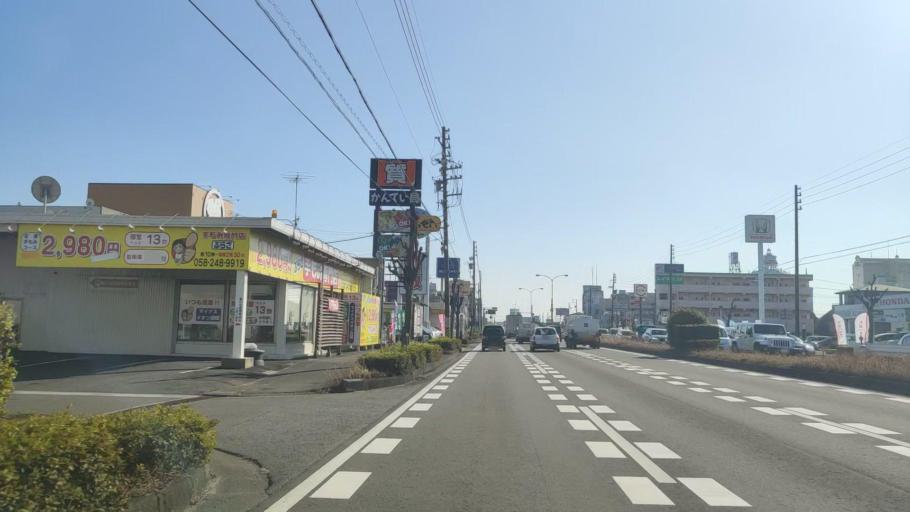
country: JP
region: Gifu
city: Gifu-shi
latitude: 35.4089
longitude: 136.7850
